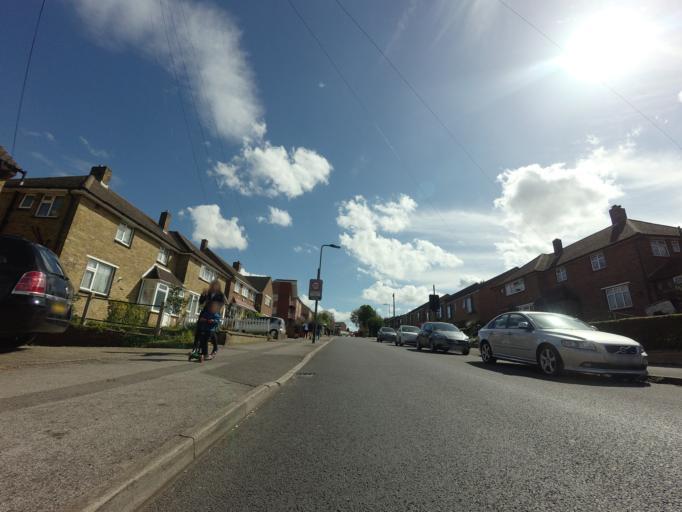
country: GB
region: England
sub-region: Greater London
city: Orpington
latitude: 51.3765
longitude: 0.1160
